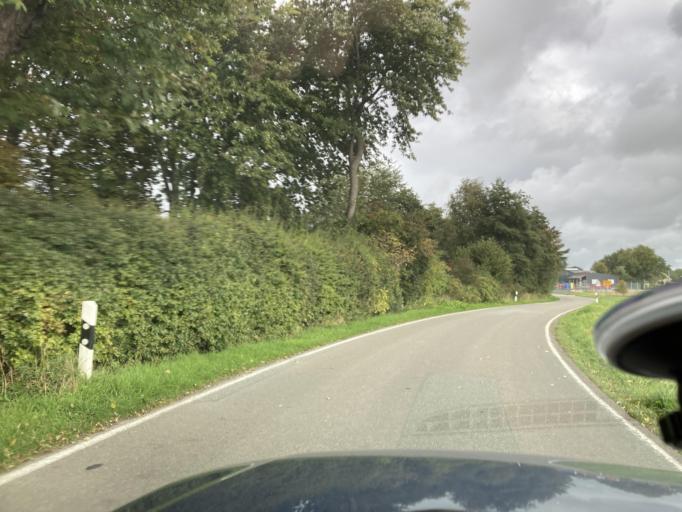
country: DE
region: Schleswig-Holstein
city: Wesselburener Deichhausen
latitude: 54.1747
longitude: 8.9333
